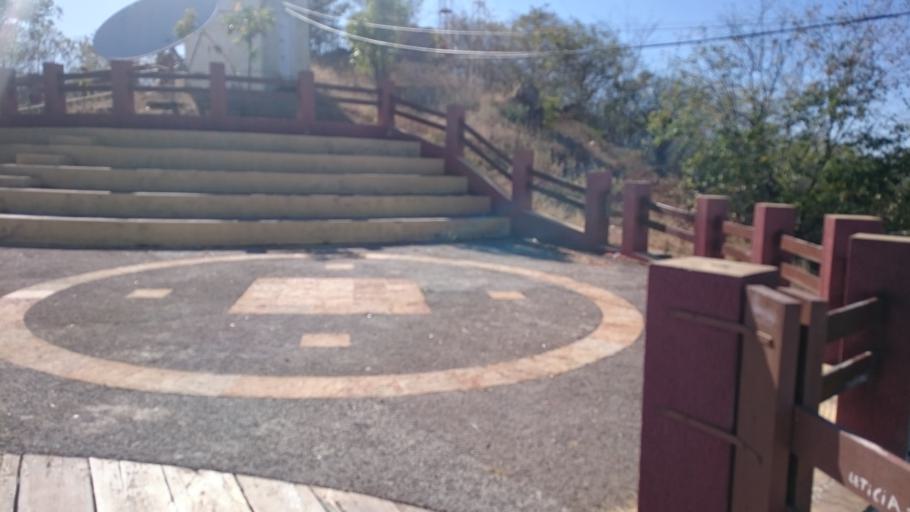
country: BR
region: Paraiba
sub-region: Catole Do Rocha
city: Sao Bento
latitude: -6.1516
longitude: -37.7646
